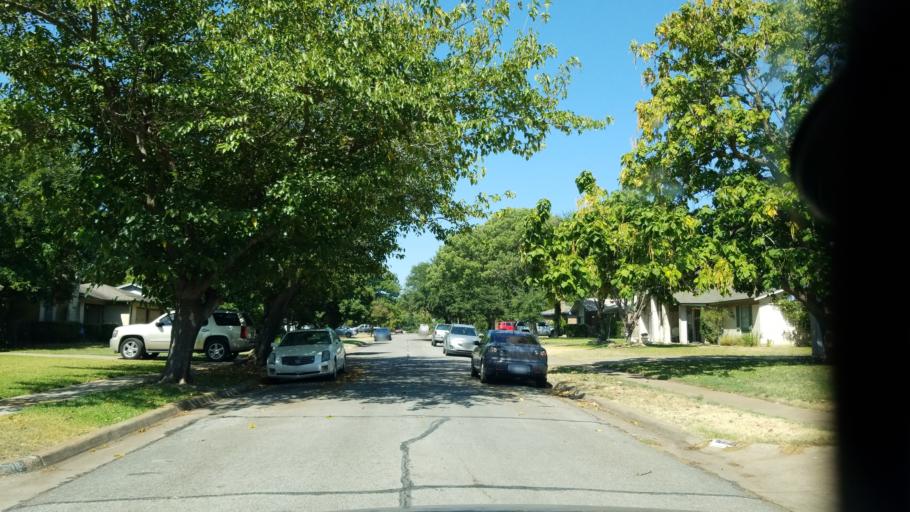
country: US
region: Texas
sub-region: Dallas County
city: Duncanville
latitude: 32.6413
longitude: -96.8998
